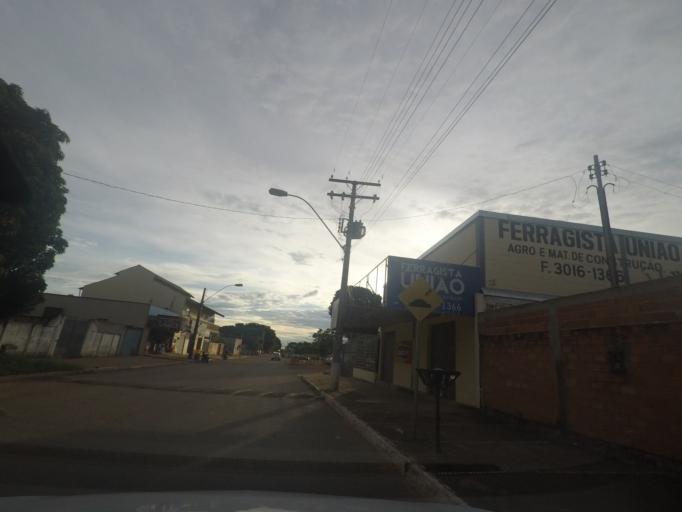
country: BR
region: Goias
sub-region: Trindade
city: Trindade
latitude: -16.7204
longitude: -49.4350
